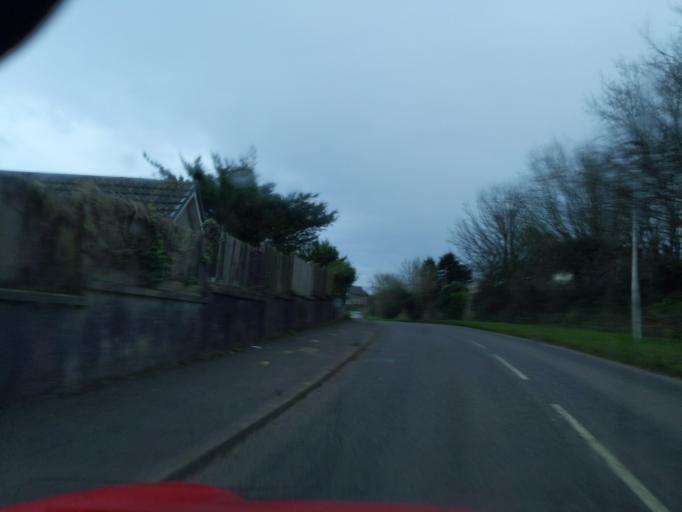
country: GB
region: England
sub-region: Devon
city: Wembury
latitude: 50.3369
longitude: -4.0729
